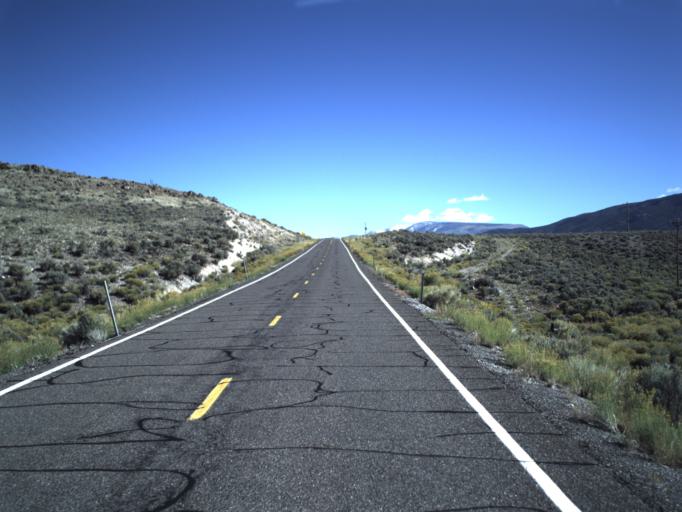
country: US
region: Utah
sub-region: Piute County
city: Junction
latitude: 38.3559
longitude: -111.9451
